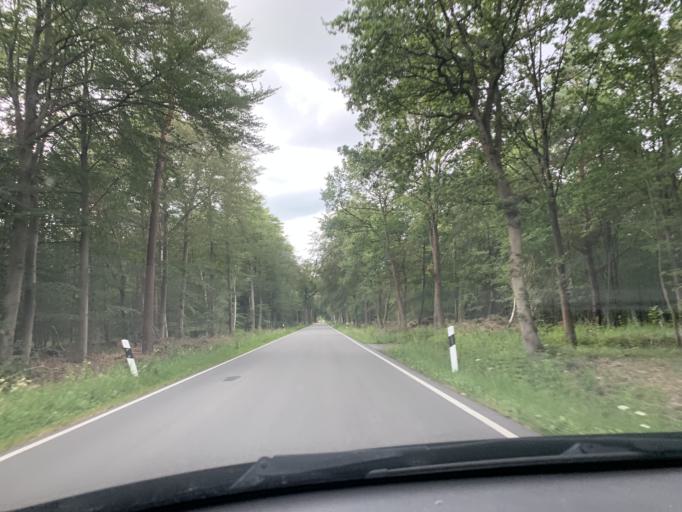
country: DE
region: Lower Saxony
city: Westerstede
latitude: 53.2178
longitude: 7.9150
